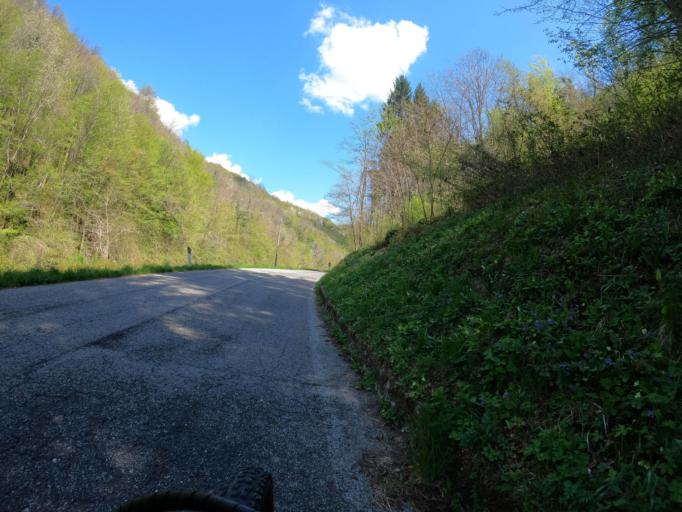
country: IT
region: Friuli Venezia Giulia
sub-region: Provincia di Udine
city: Stregna
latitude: 46.1288
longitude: 13.5702
